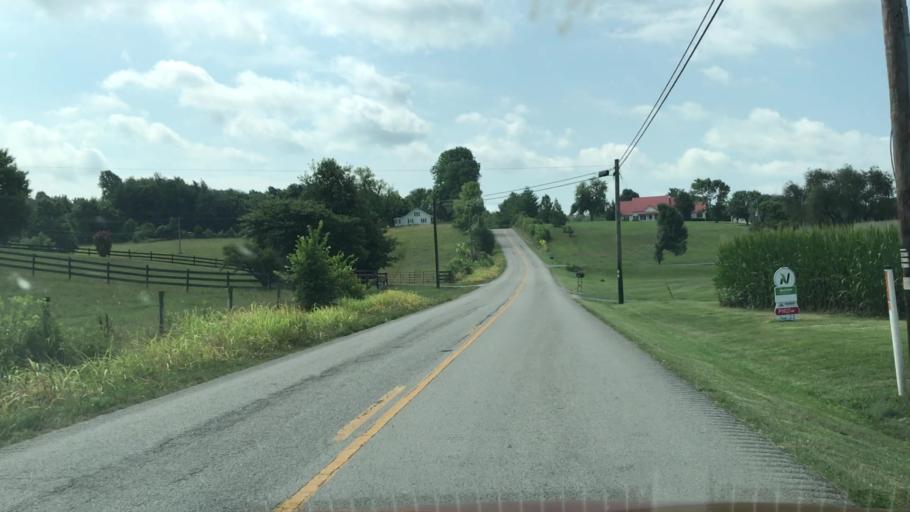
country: US
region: Kentucky
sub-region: Barren County
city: Glasgow
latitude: 36.9677
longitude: -85.8922
